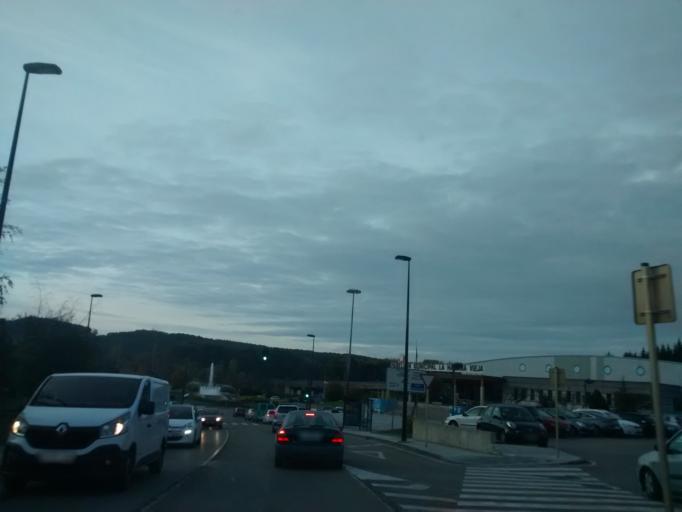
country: ES
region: Cantabria
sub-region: Provincia de Cantabria
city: Torrelavega
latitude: 43.3558
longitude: -4.0447
